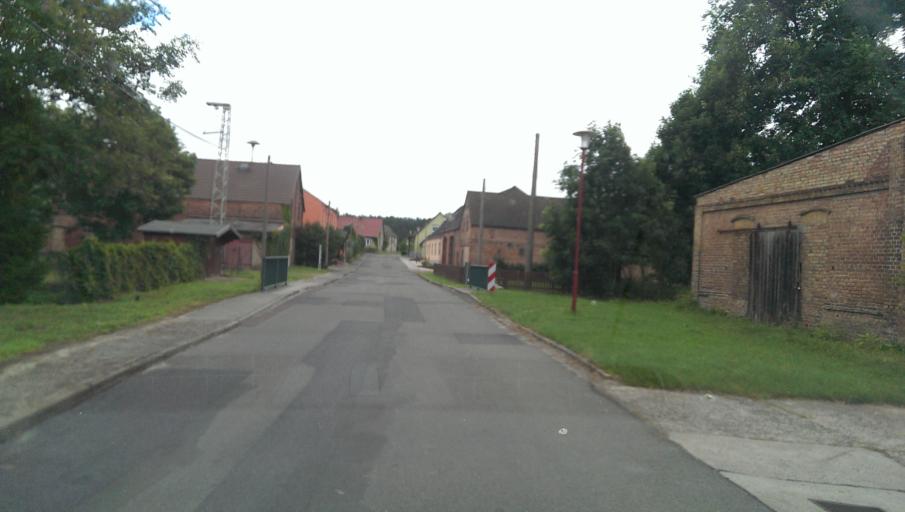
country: DE
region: Brandenburg
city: Niemegk
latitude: 52.0714
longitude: 12.6199
